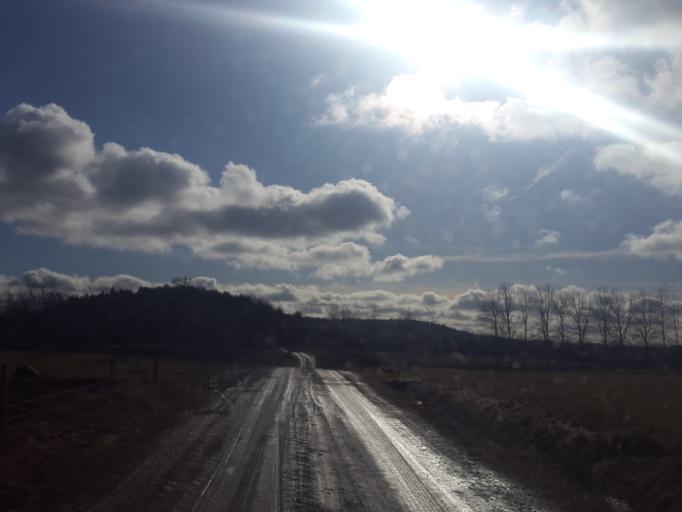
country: SE
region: Vaestra Goetaland
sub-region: Lerums Kommun
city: Olstorp
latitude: 57.8328
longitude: 12.2203
